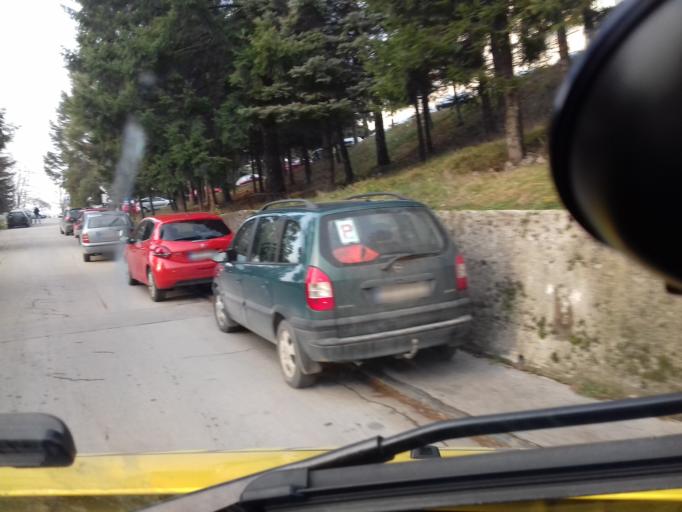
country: BA
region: Federation of Bosnia and Herzegovina
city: Zenica
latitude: 44.2104
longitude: 17.9259
